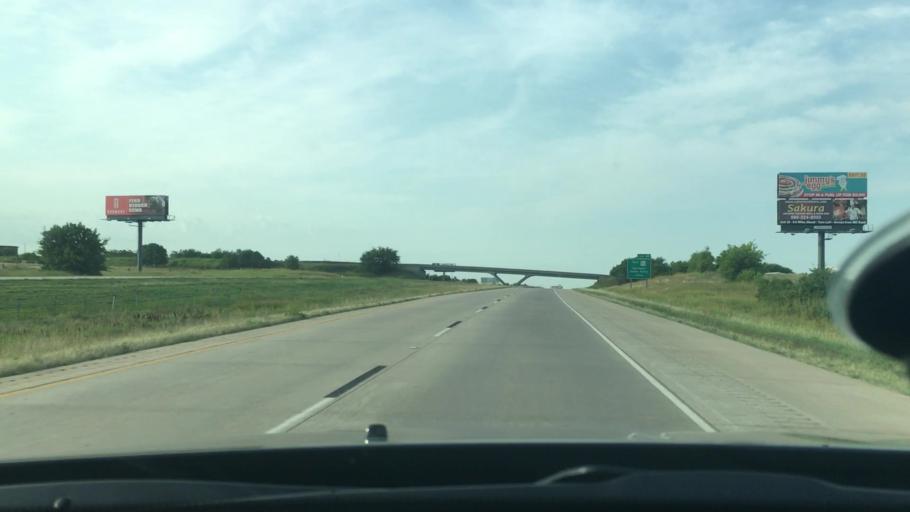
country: US
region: Oklahoma
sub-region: Carter County
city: Ardmore
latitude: 34.3215
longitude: -97.1560
